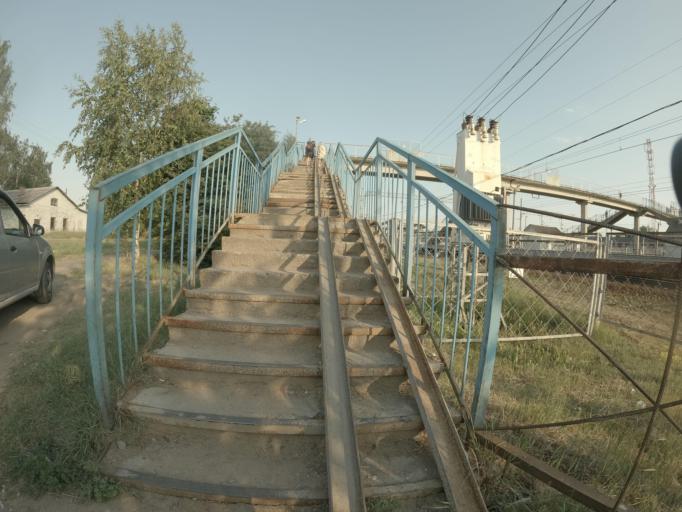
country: RU
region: Leningrad
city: Yakovlevo
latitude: 60.4680
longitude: 29.2848
